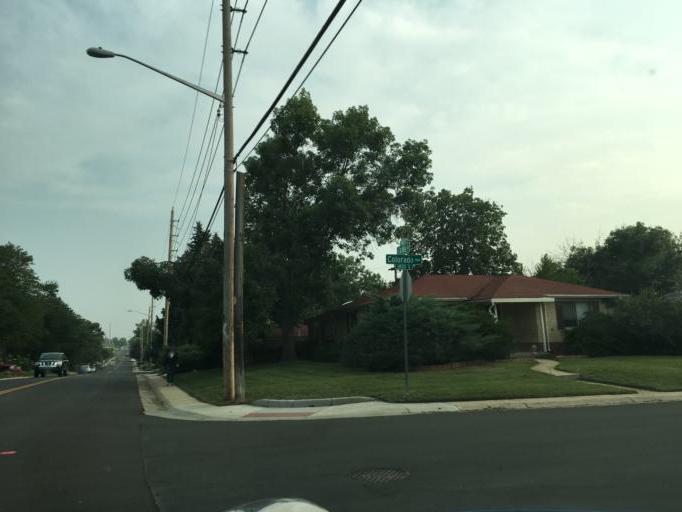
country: US
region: Colorado
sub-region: Arapahoe County
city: Glendale
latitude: 39.6844
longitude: -104.9317
